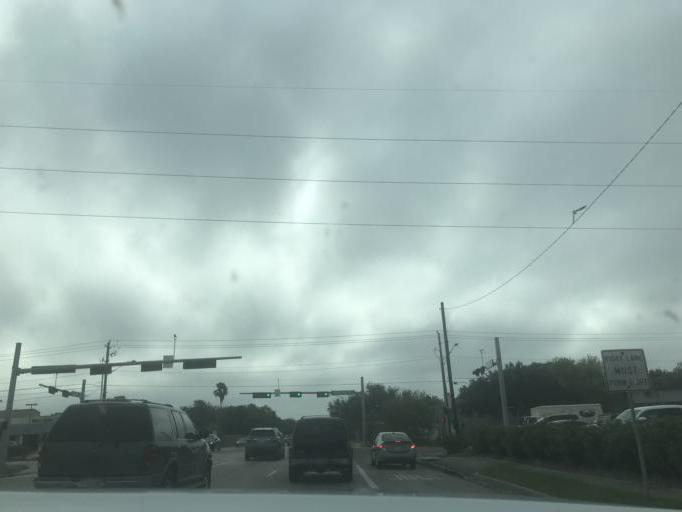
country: US
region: Texas
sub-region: Nueces County
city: Corpus Christi
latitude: 27.6853
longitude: -97.3654
